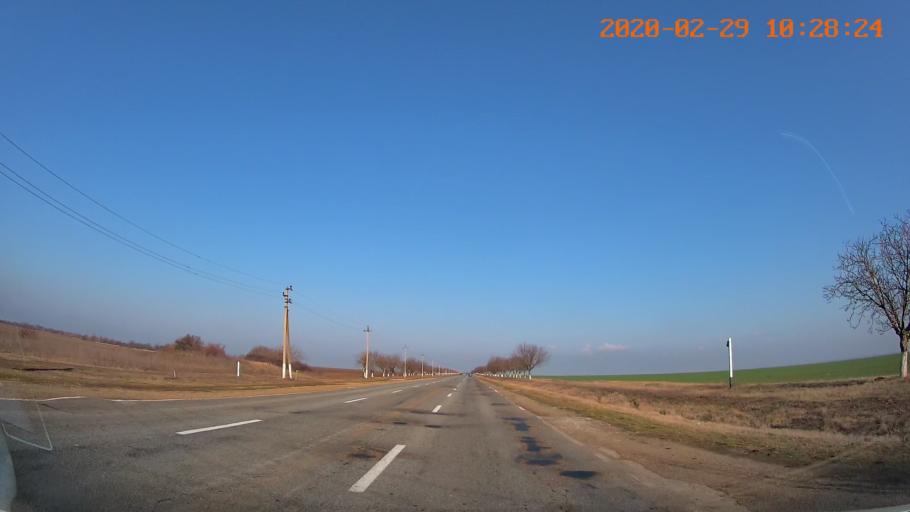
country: MD
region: Telenesti
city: Tiraspolul Nou
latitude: 46.9100
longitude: 29.5916
